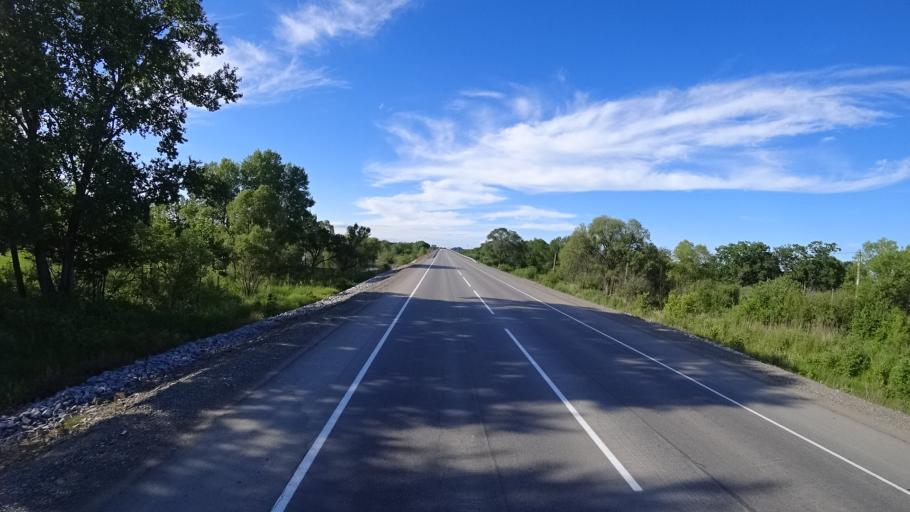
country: RU
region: Khabarovsk Krai
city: Khor
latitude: 47.8581
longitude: 134.9624
